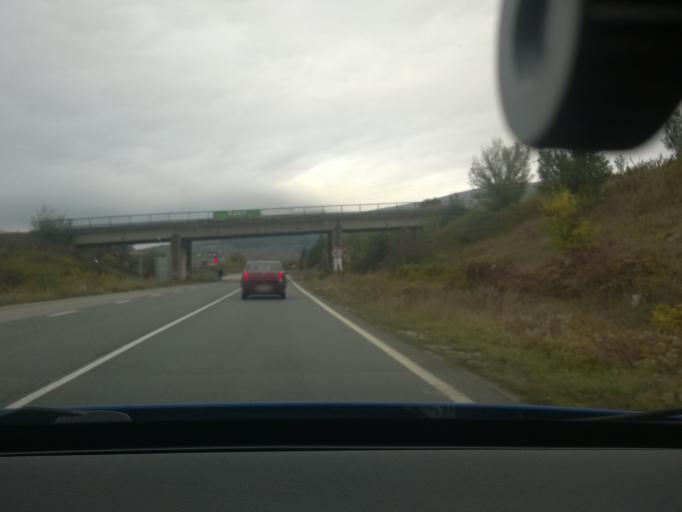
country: BG
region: Sofiya
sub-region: Obshtina Dragoman
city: Dragoman
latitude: 42.9236
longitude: 22.9367
